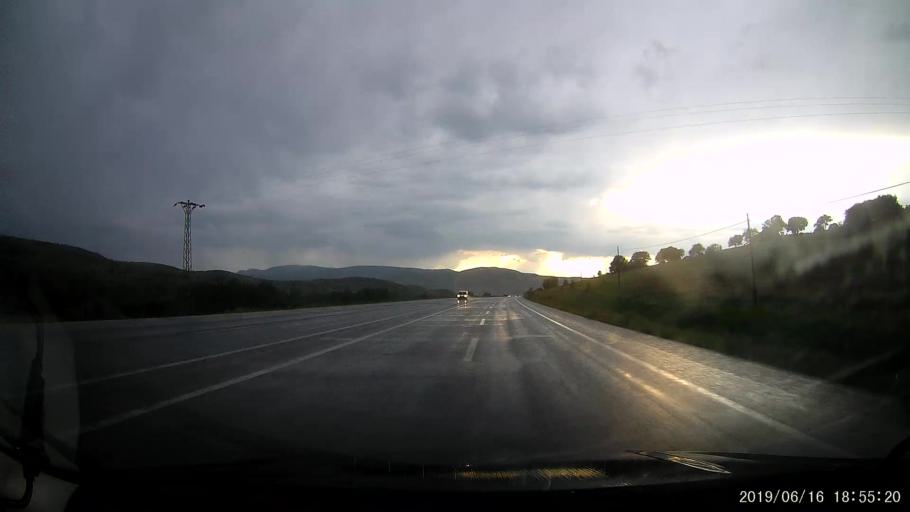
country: TR
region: Erzincan
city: Refahiye
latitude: 39.8996
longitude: 38.8303
